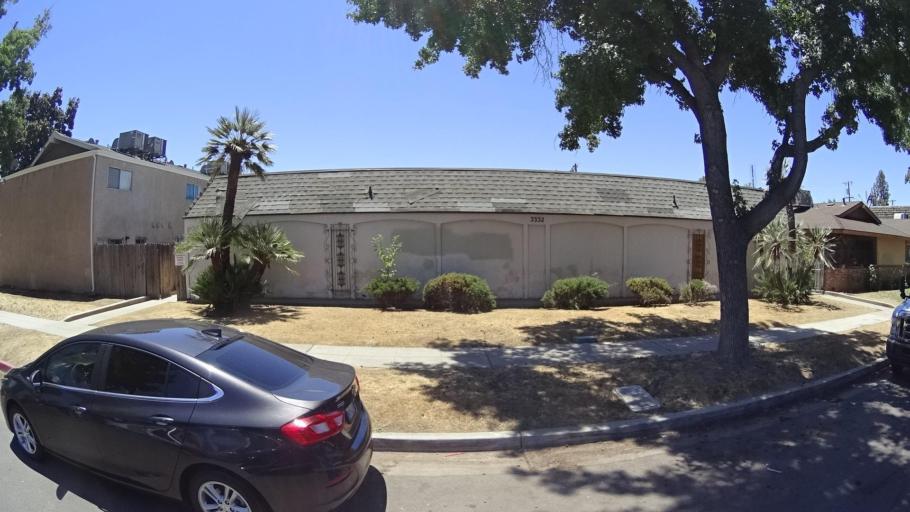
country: US
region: California
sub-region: Fresno County
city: Fresno
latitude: 36.8075
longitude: -119.7687
